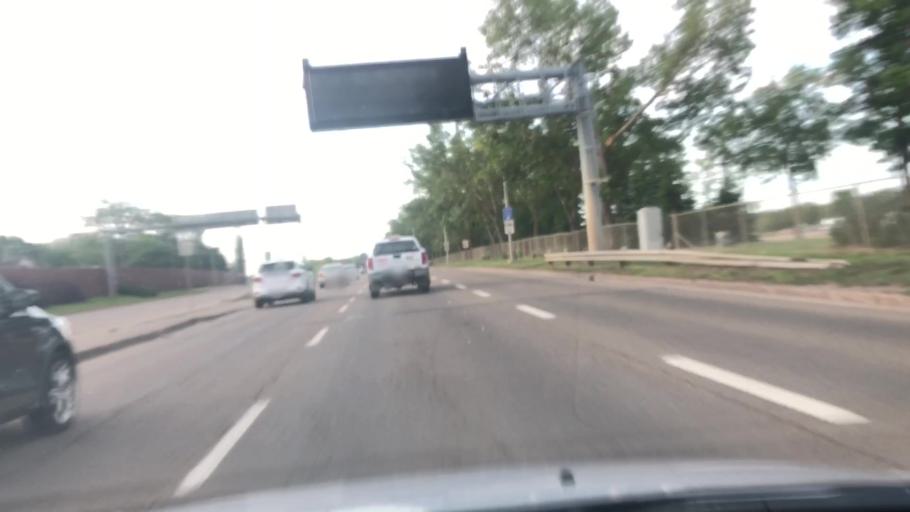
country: CA
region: Alberta
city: Edmonton
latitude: 53.5670
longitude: -113.4506
